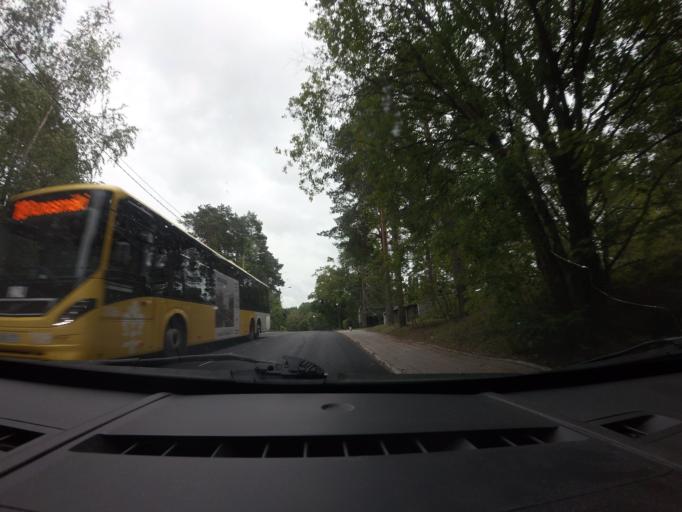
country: FI
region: Varsinais-Suomi
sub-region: Turku
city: Turku
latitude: 60.4324
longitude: 22.2779
